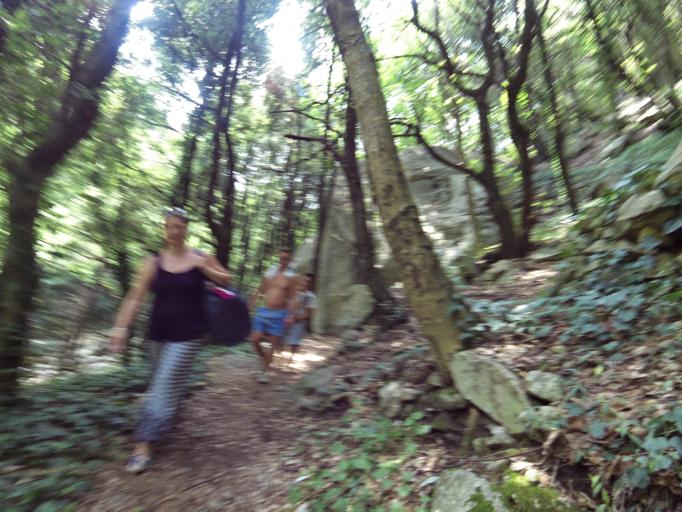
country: IT
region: Calabria
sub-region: Provincia di Reggio Calabria
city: Bivongi
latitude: 38.5020
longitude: 16.3983
